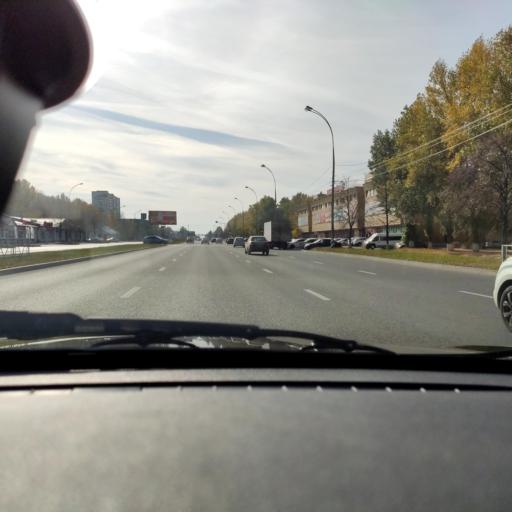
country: RU
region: Samara
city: Tol'yatti
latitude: 53.5350
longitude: 49.2830
